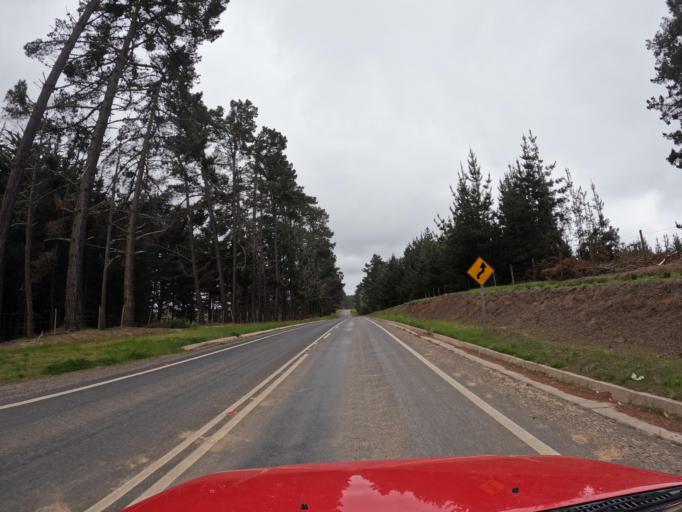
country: CL
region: O'Higgins
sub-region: Provincia de Colchagua
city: Santa Cruz
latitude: -34.5636
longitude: -72.0164
